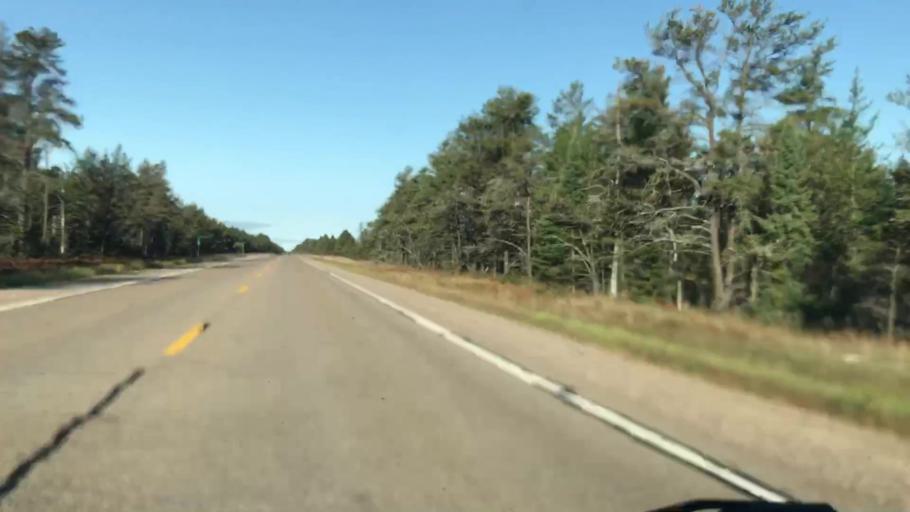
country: US
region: Michigan
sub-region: Chippewa County
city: Sault Ste. Marie
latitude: 46.3587
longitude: -84.8214
